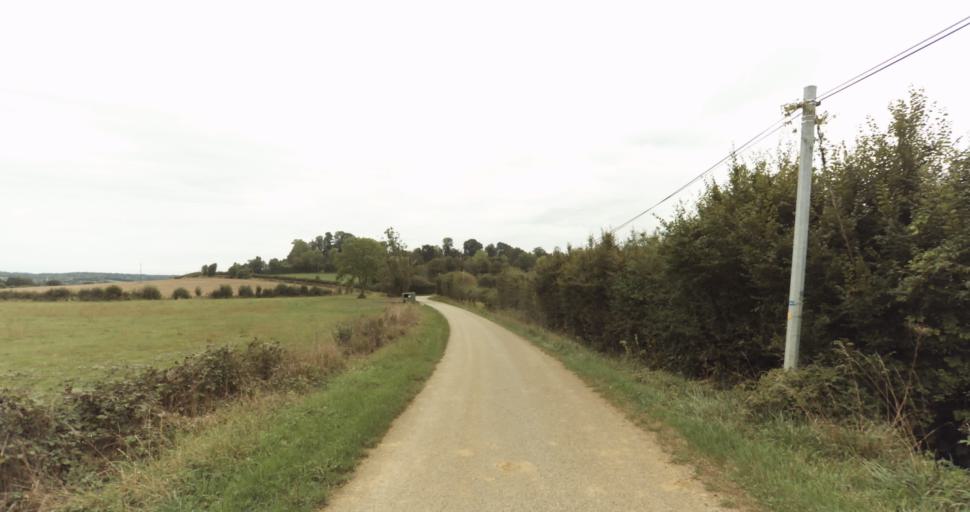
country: FR
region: Lower Normandy
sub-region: Departement de l'Orne
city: Gace
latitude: 48.7503
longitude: 0.3373
